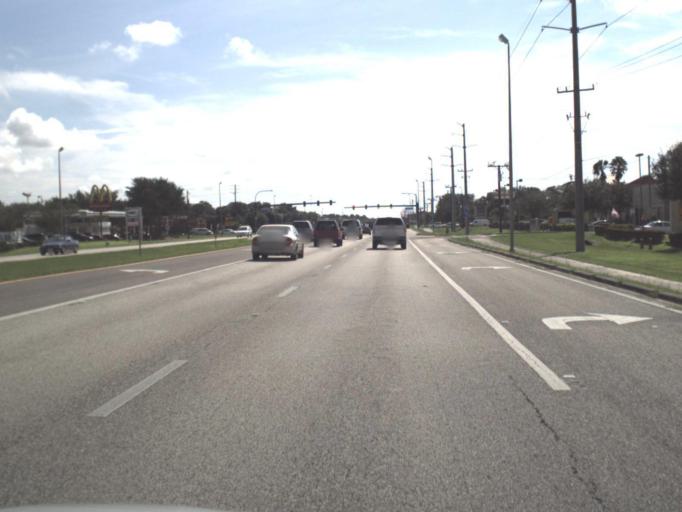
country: US
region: Florida
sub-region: Sarasota County
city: North Port
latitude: 27.0389
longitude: -82.2224
